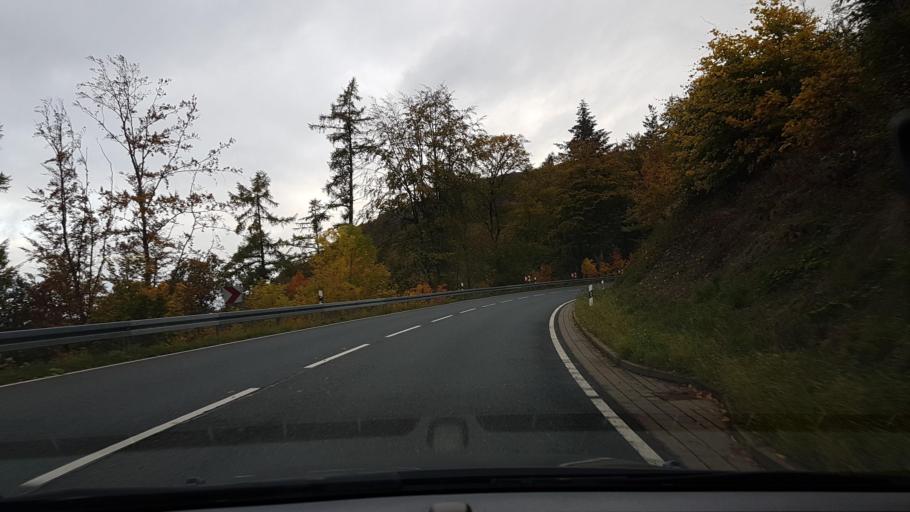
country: DE
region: Lower Saxony
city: Bad Grund
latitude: 51.8116
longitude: 10.2458
